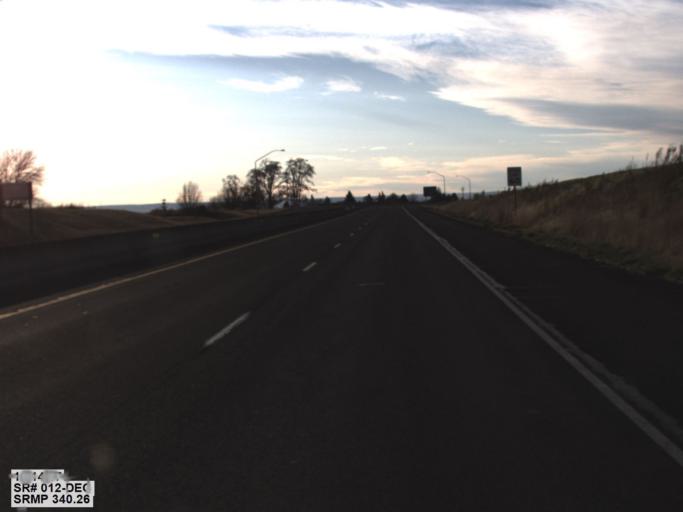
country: US
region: Washington
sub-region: Walla Walla County
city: Walla Walla East
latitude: 46.0852
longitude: -118.2735
